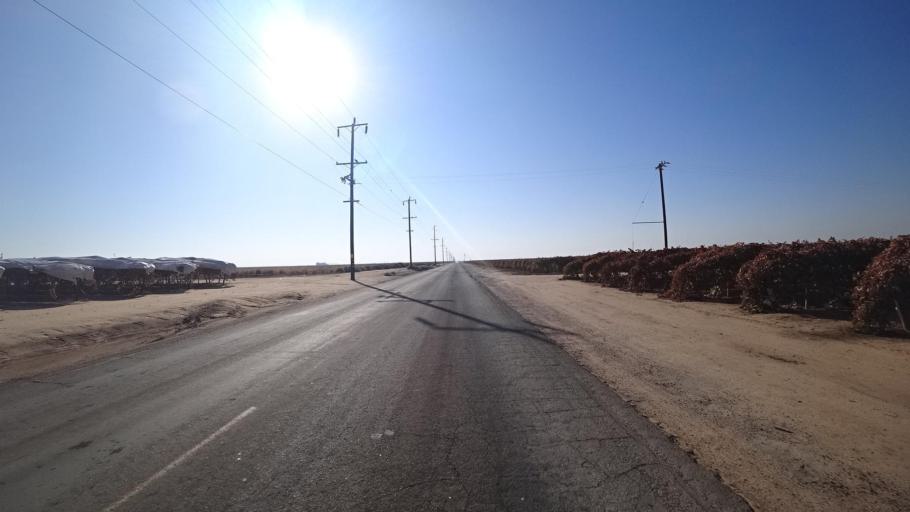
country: US
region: California
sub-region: Kern County
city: Delano
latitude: 35.7436
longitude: -119.2052
